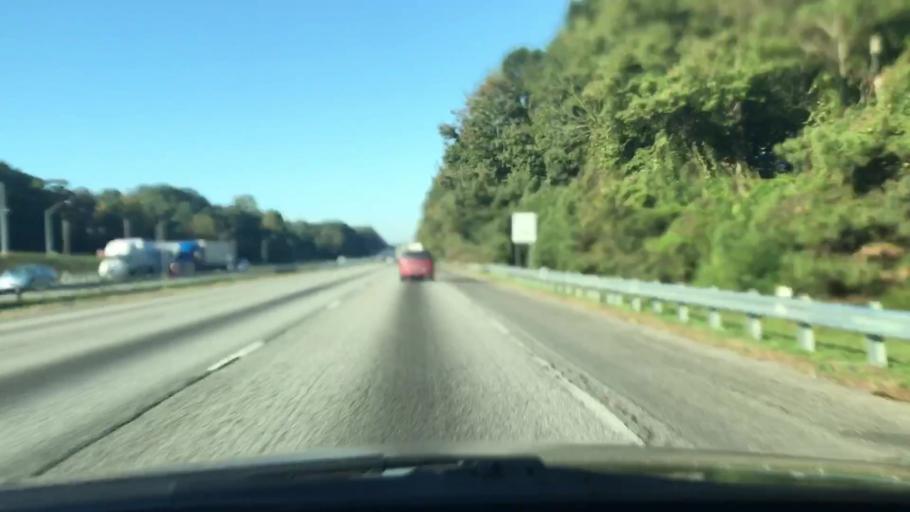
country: US
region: Georgia
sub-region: Douglas County
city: Lithia Springs
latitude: 33.7734
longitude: -84.6301
